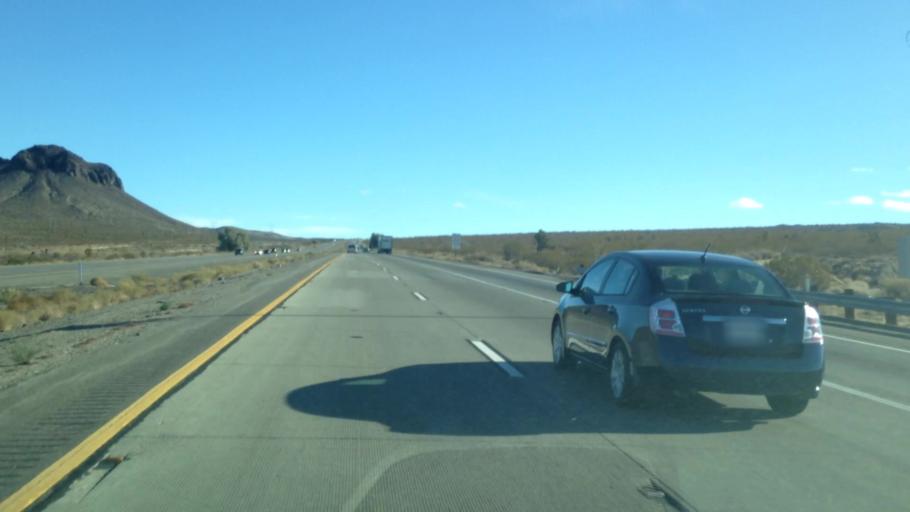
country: US
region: Nevada
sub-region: Clark County
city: Sandy Valley
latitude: 35.3872
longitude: -115.8495
